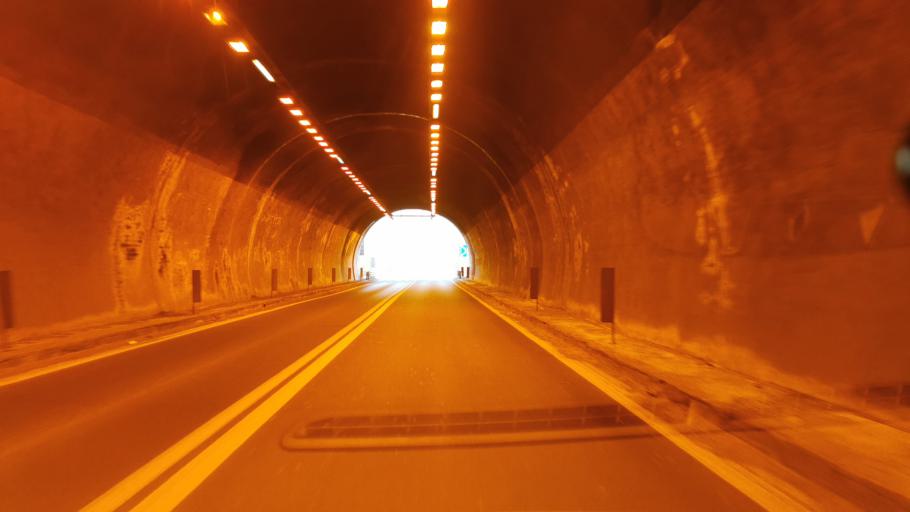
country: IT
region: Piedmont
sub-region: Provincia di Torino
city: Baldissero Canavese
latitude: 45.4060
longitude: 7.7561
